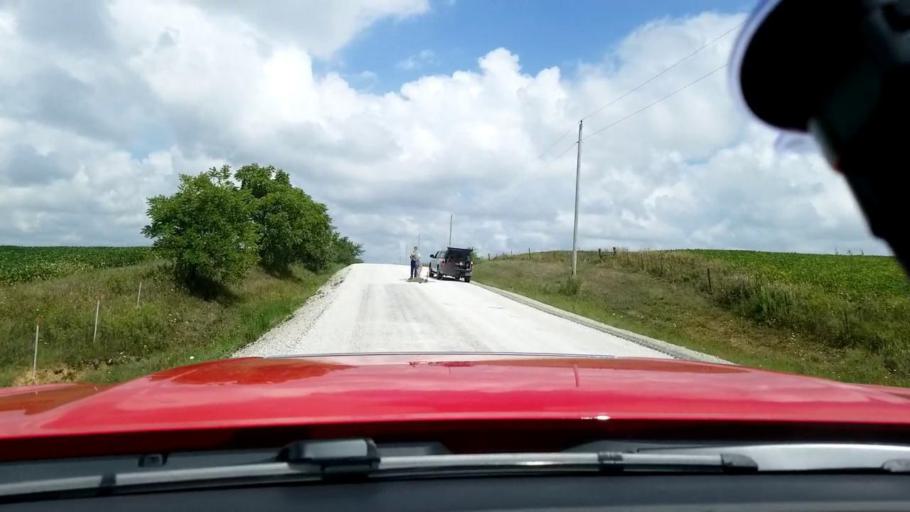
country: US
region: Iowa
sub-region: Decatur County
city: Lamoni
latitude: 40.6634
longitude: -94.0483
